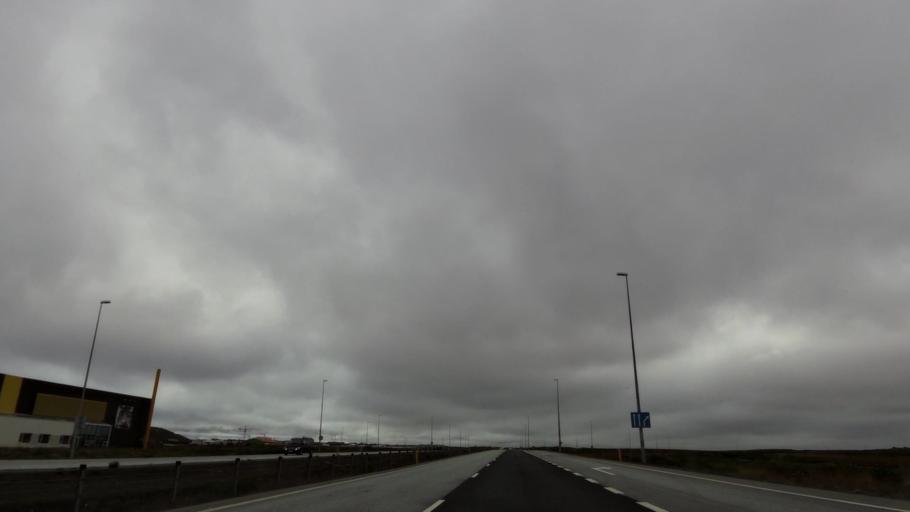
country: IS
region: Southern Peninsula
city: Reykjanesbaer
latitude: 63.9691
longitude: -22.5192
